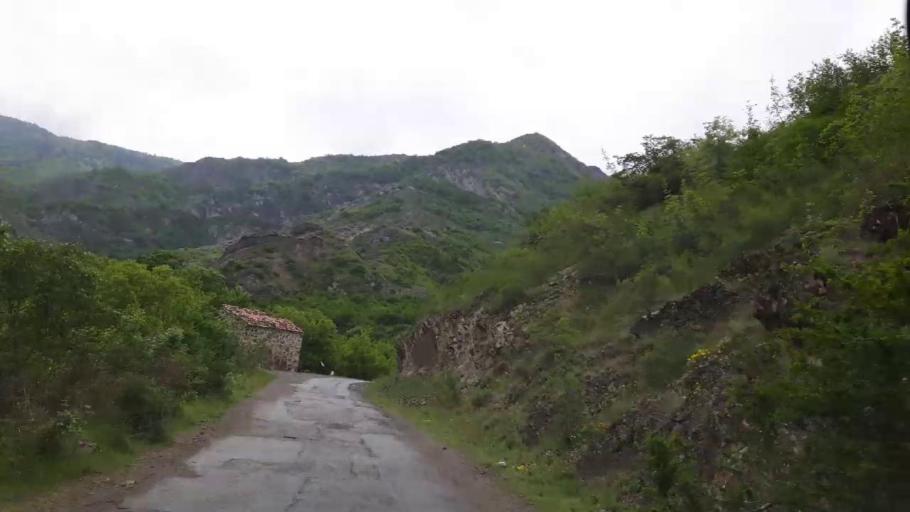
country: GE
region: Shida Kartli
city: Gori
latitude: 41.9021
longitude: 44.0918
